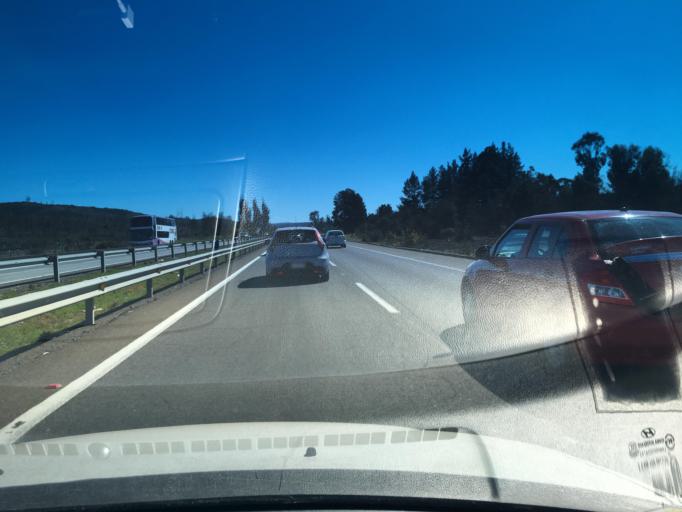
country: CL
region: Valparaiso
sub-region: Provincia de Marga Marga
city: Quilpue
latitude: -33.1947
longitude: -71.4944
